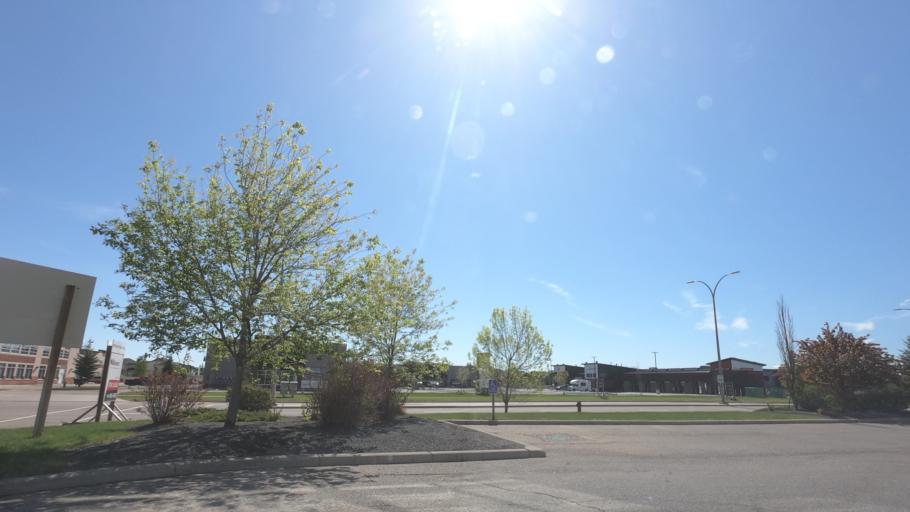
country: CA
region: Alberta
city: Airdrie
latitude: 51.2616
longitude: -113.9959
